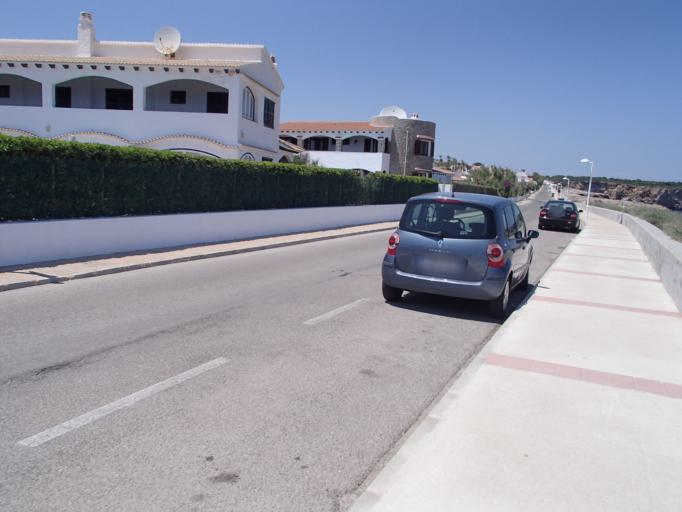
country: ES
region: Balearic Islands
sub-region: Illes Balears
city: Es Castell
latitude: 39.8340
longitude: 4.3026
